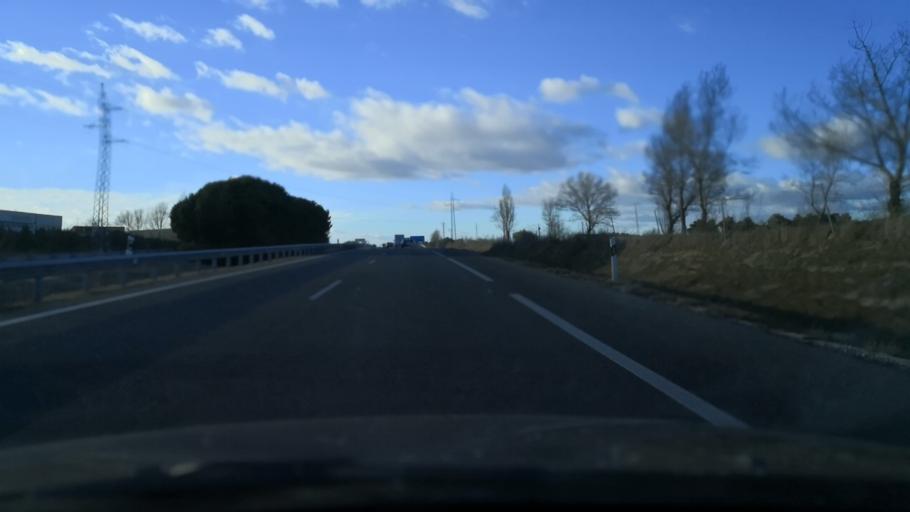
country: ES
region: Castille and Leon
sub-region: Provincia de Avila
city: Arevalo
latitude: 41.0750
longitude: -4.7239
